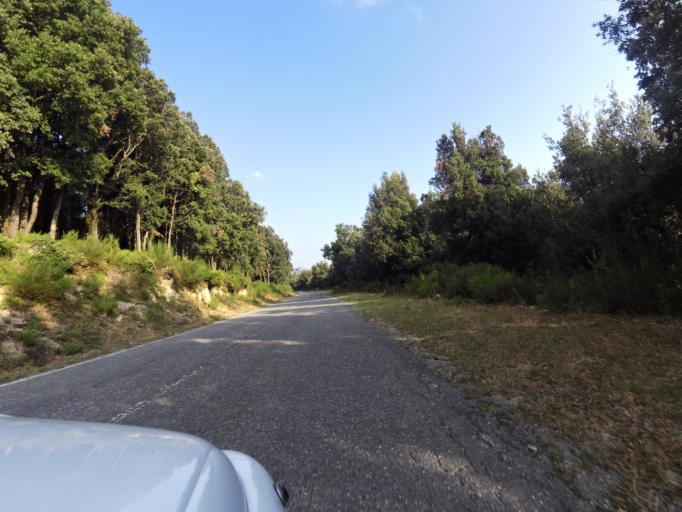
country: IT
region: Calabria
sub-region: Provincia di Reggio Calabria
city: Pazzano
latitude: 38.4747
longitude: 16.4003
